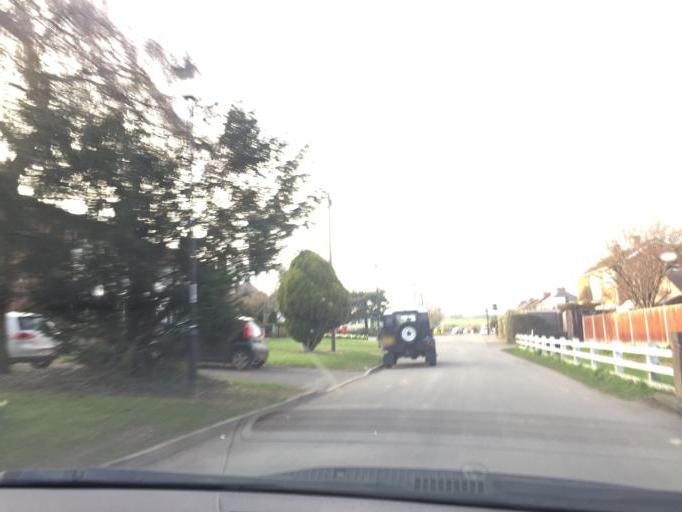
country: GB
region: England
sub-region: Coventry
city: Keresley
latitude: 52.4306
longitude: -1.5677
